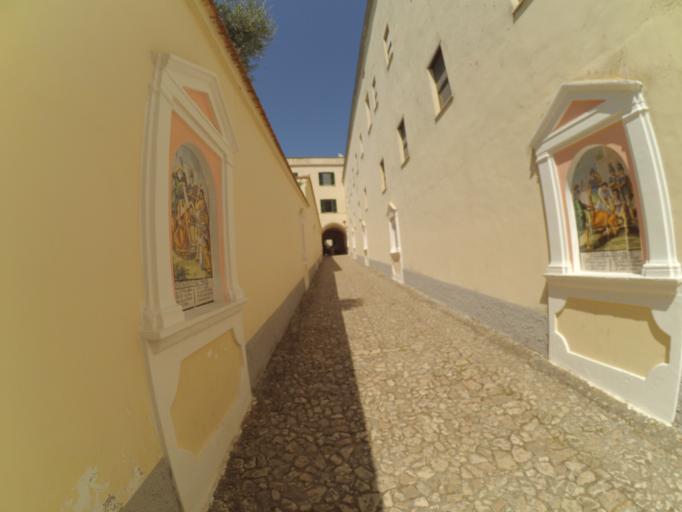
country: IT
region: Latium
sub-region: Provincia di Latina
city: Gaeta
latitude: 41.2052
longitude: 13.5704
